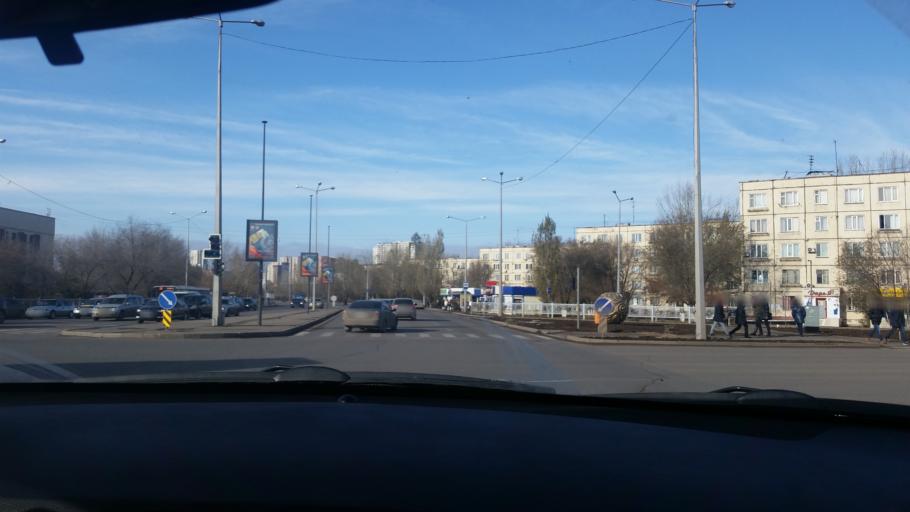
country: KZ
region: Astana Qalasy
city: Astana
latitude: 51.1551
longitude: 71.4538
